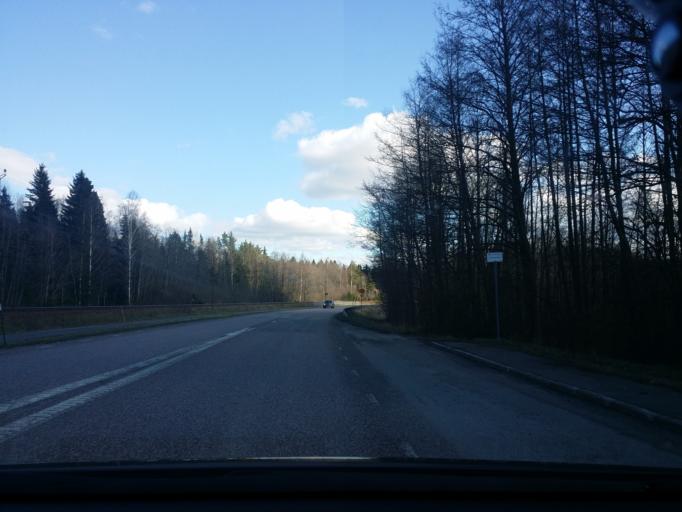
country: SE
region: Vaestmanland
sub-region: Sala Kommun
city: Sala
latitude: 59.9472
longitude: 16.5426
